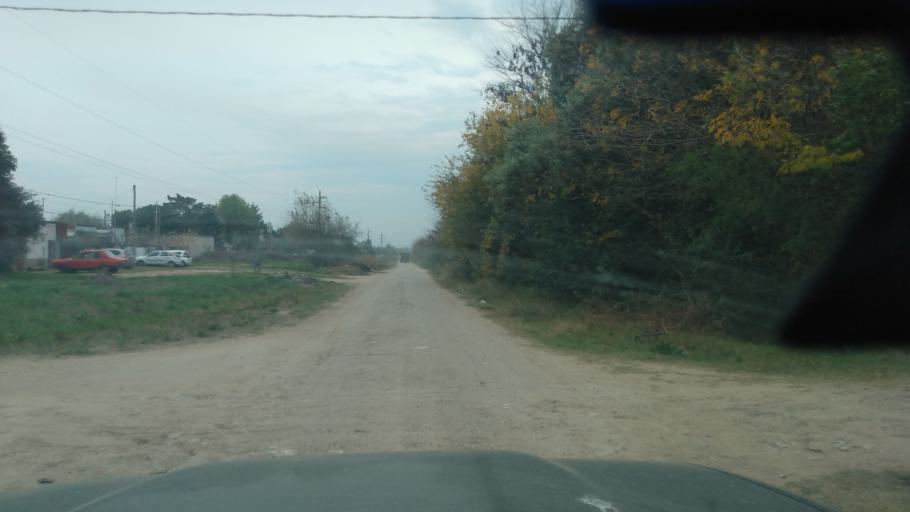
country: AR
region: Buenos Aires
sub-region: Partido de Lujan
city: Lujan
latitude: -34.5605
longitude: -59.1447
